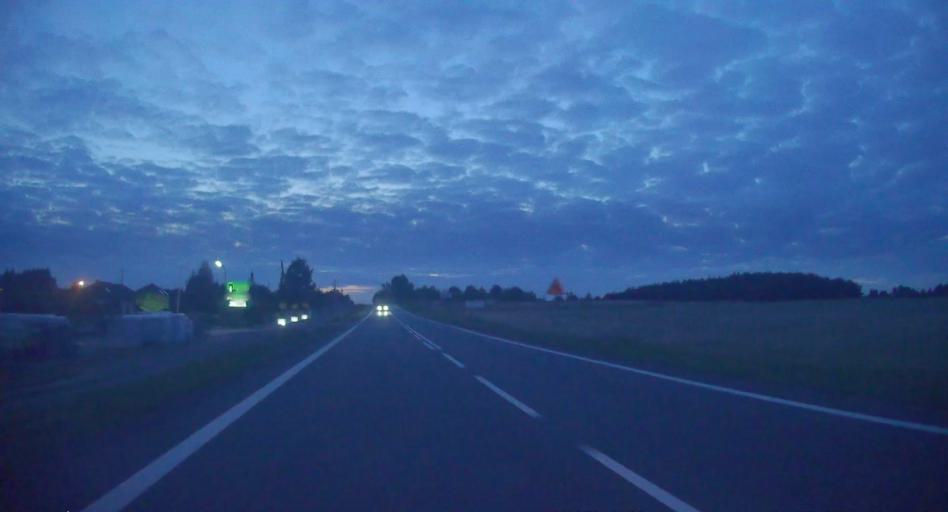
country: PL
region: Silesian Voivodeship
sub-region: Powiat klobucki
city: Kamyk
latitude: 50.8790
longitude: 18.9964
